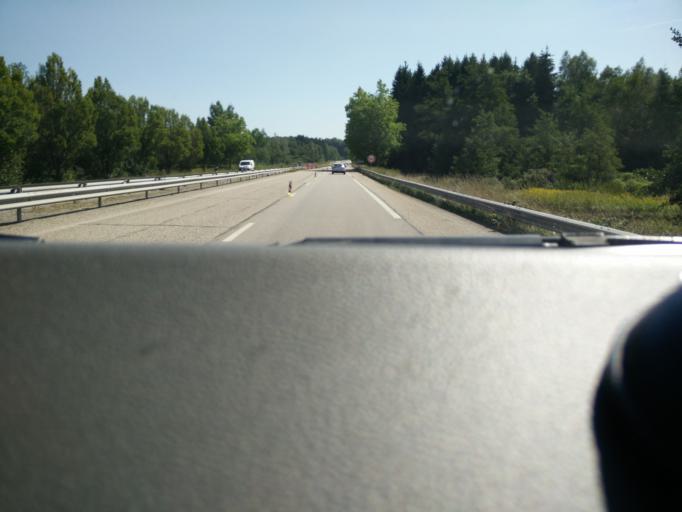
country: FR
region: Lorraine
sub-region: Departement des Vosges
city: Saint-Michel-sur-Meurthe
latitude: 48.3497
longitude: 6.8855
